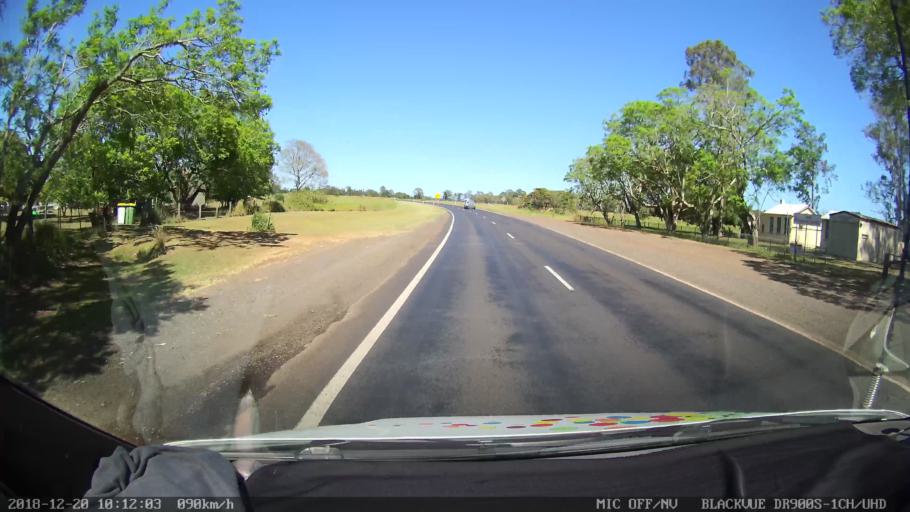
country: AU
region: New South Wales
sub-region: Richmond Valley
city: Casino
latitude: -28.8717
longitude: 153.1494
